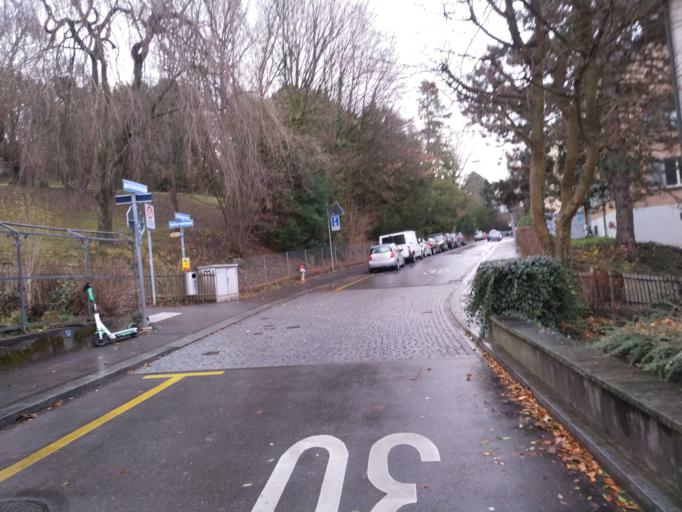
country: CH
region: Zurich
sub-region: Bezirk Zuerich
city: Zuerich (Kreis 2) / Enge
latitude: 47.3592
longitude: 8.5286
